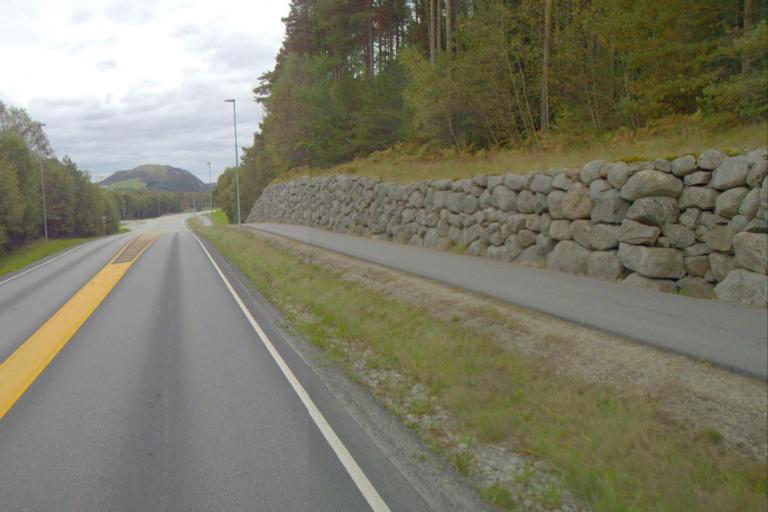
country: NO
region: Rogaland
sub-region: Sandnes
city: Hommersak
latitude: 58.8849
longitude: 5.8390
